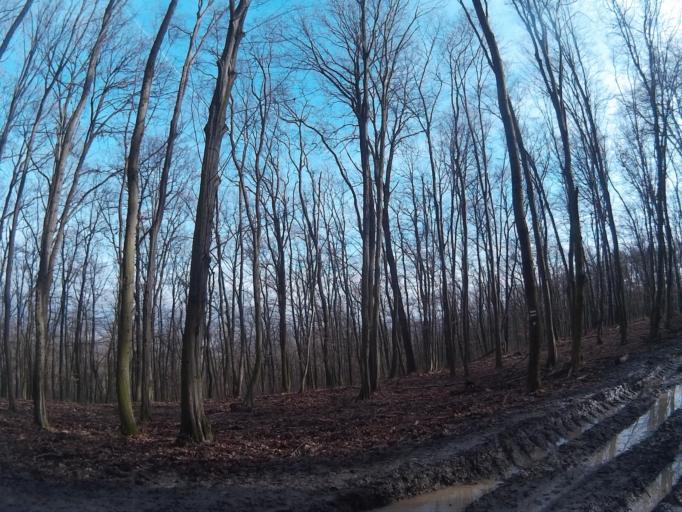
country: HU
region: Komarom-Esztergom
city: Tarjan
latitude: 47.6100
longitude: 18.4767
